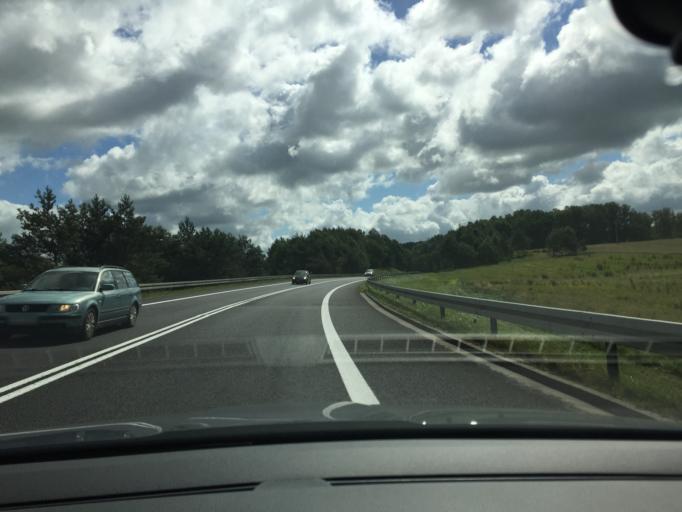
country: PL
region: West Pomeranian Voivodeship
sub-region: Powiat slawienski
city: Darlowo
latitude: 54.2780
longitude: 16.4408
